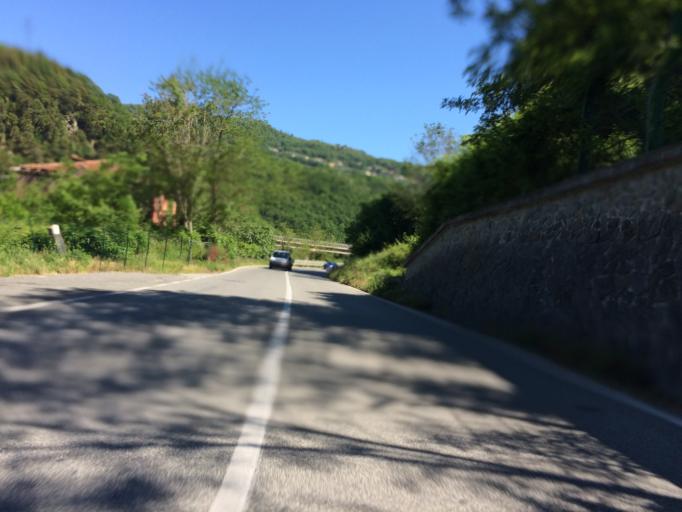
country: IT
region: Tuscany
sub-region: Provincia di Massa-Carrara
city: Podenzana
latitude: 44.1917
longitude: 9.9420
